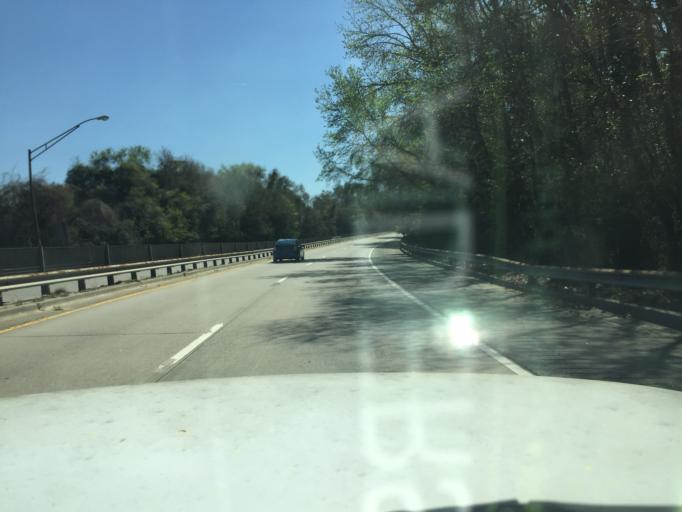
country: US
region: Georgia
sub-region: Chatham County
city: Savannah
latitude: 32.0644
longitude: -81.1120
